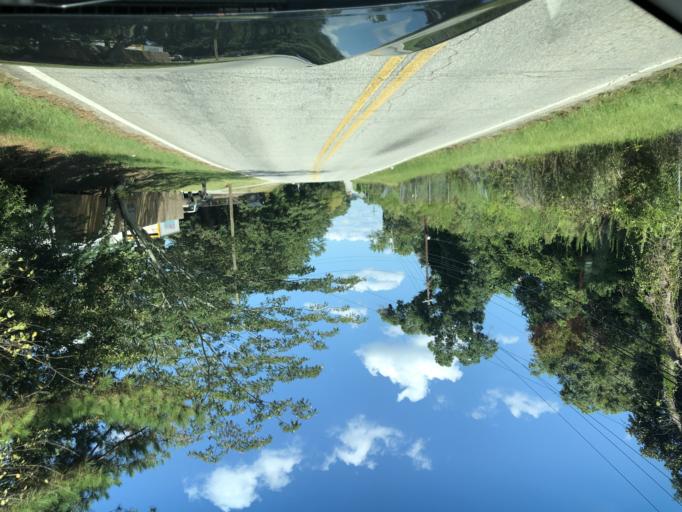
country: US
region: Georgia
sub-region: Muscogee County
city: Columbus
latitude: 32.5154
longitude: -84.9225
